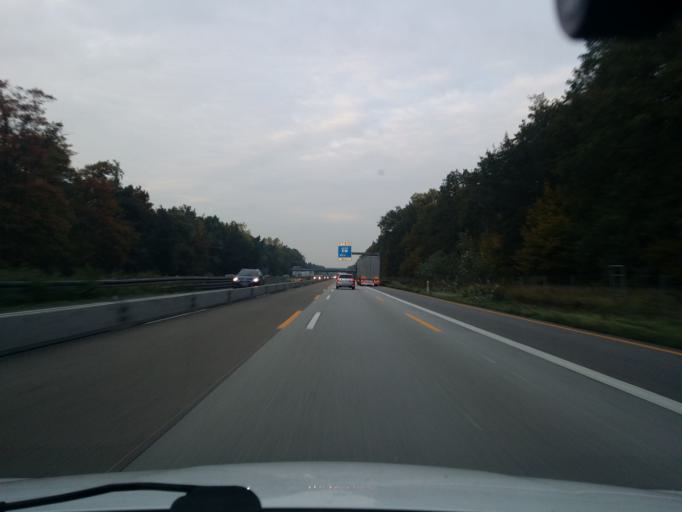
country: DE
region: Hesse
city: Lorsch
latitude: 49.6348
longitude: 8.5542
